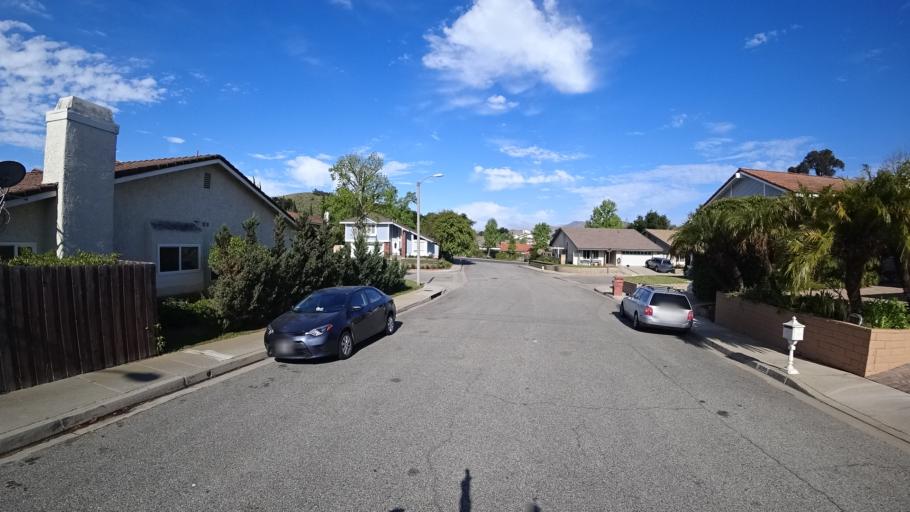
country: US
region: California
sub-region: Ventura County
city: Casa Conejo
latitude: 34.1710
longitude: -118.9415
